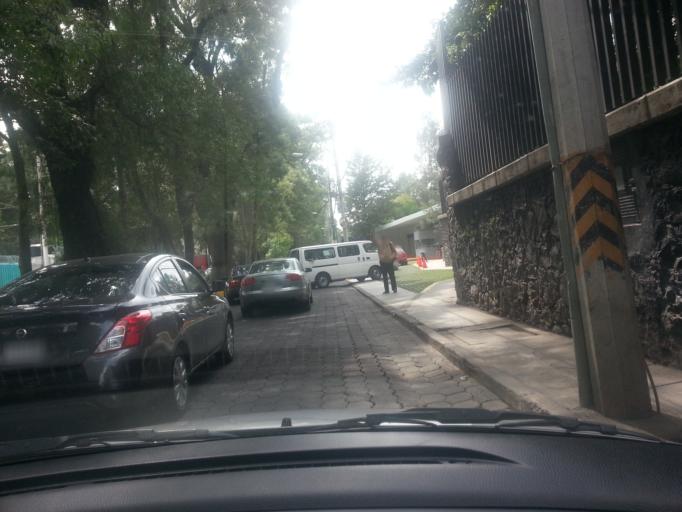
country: MX
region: Mexico City
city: Tlalpan
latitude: 19.2958
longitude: -99.1859
